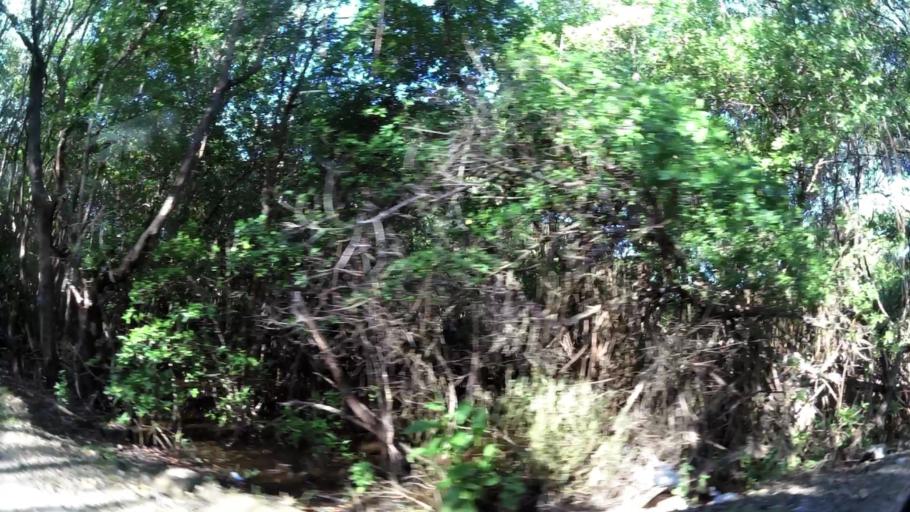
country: TT
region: Tobago
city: Scarborough
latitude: 11.1509
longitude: -60.8138
